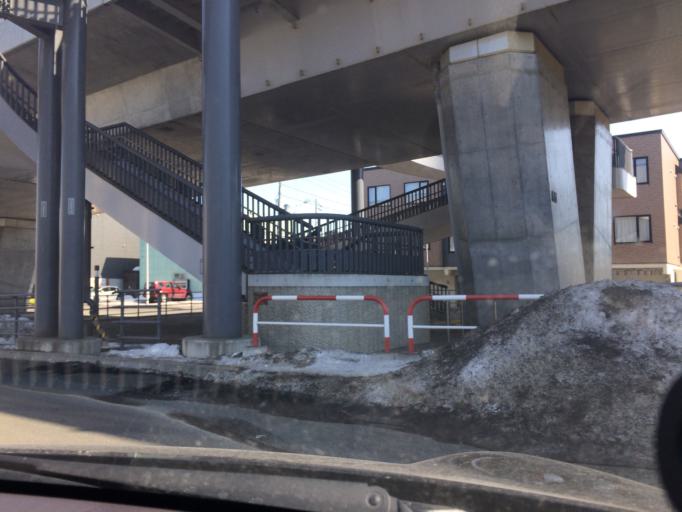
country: JP
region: Hokkaido
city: Sapporo
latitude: 43.0572
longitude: 141.4104
